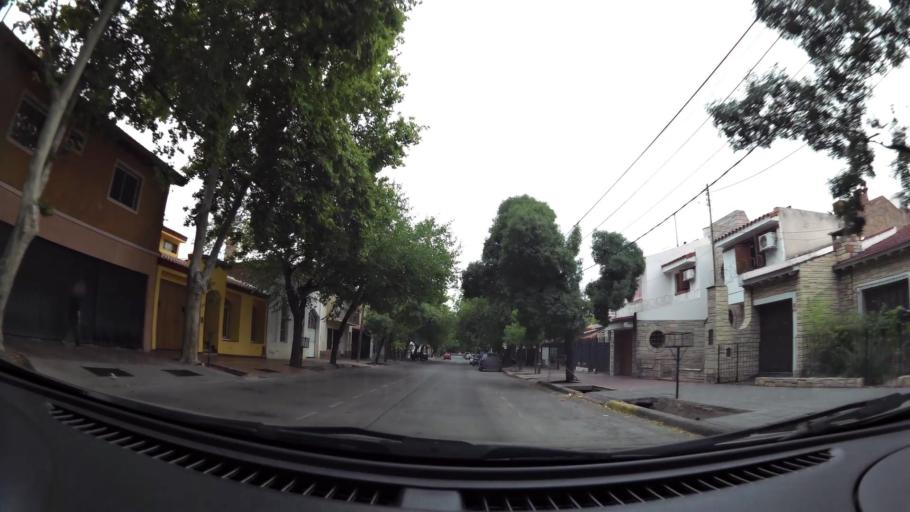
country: AR
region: Mendoza
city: Mendoza
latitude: -32.8880
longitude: -68.8615
